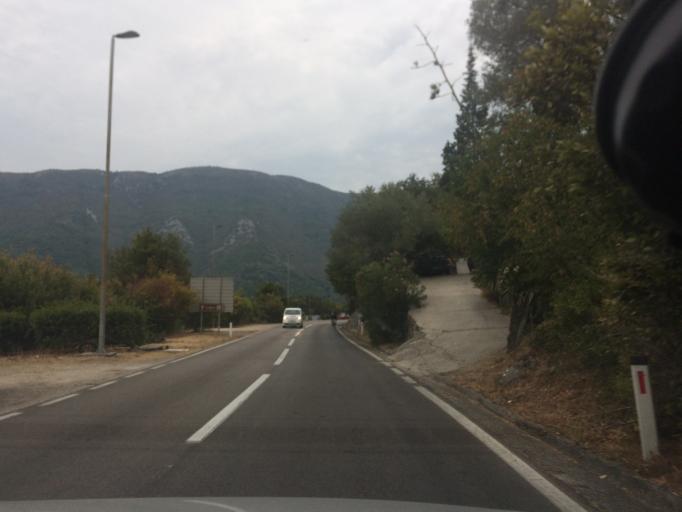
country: ME
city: Lipci
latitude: 42.5003
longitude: 18.6611
